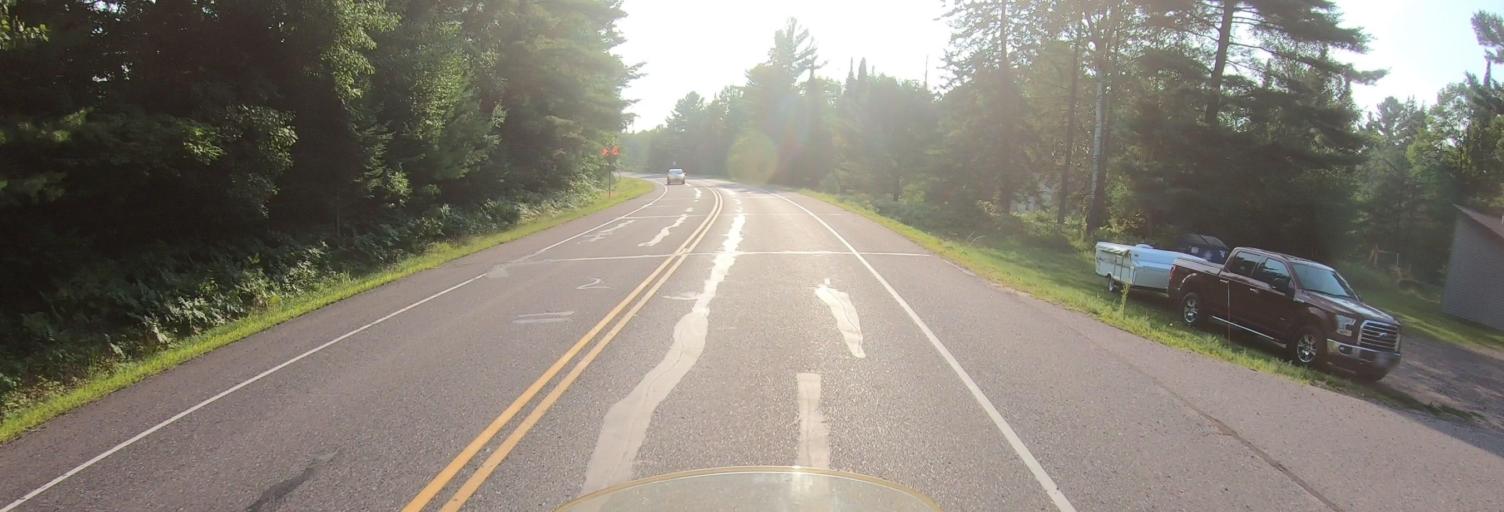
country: US
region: Wisconsin
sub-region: Ashland County
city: Ashland
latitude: 46.1672
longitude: -90.9125
